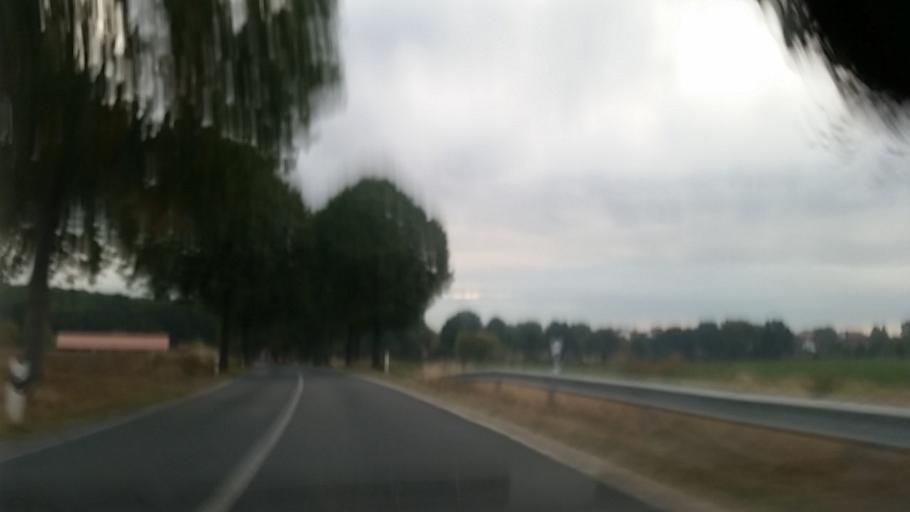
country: DE
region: Lower Saxony
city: Hankensbuttel
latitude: 52.7318
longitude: 10.5898
